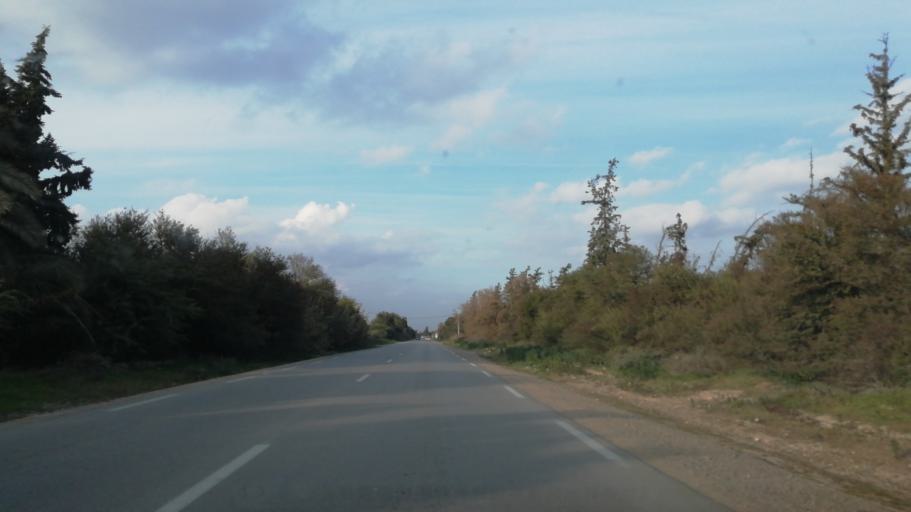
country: DZ
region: Mascara
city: Mascara
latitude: 35.6109
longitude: 0.0520
